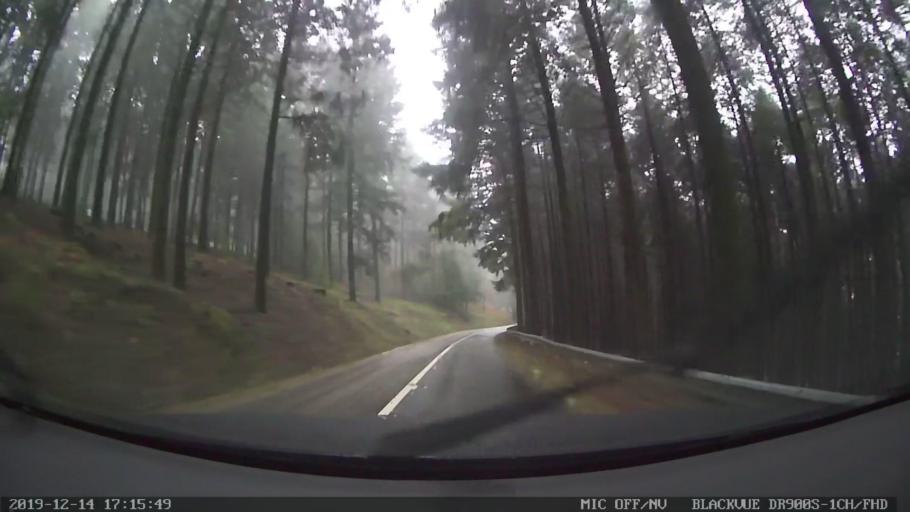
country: PT
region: Vila Real
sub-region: Vila Pouca de Aguiar
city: Vila Pouca de Aguiar
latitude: 41.5051
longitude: -7.6269
